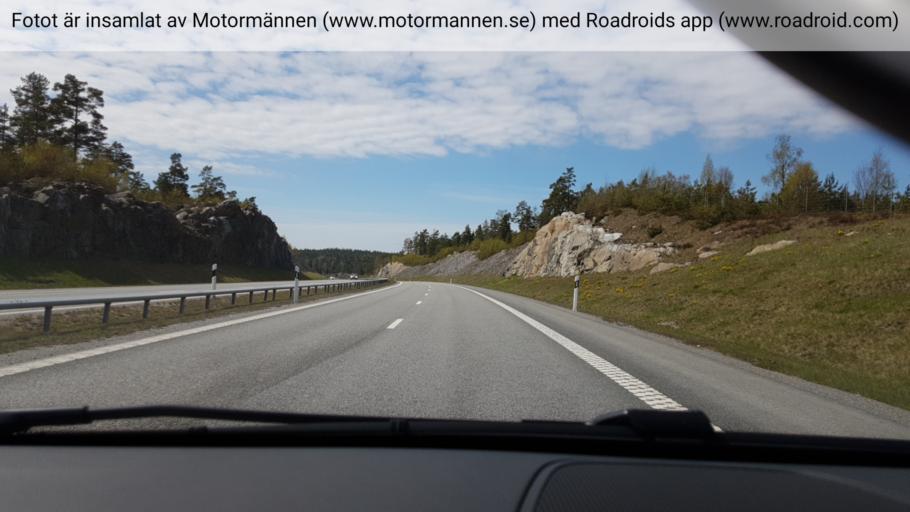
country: SE
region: Stockholm
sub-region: Nynashamns Kommun
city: Osmo
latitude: 59.0586
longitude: 18.0142
